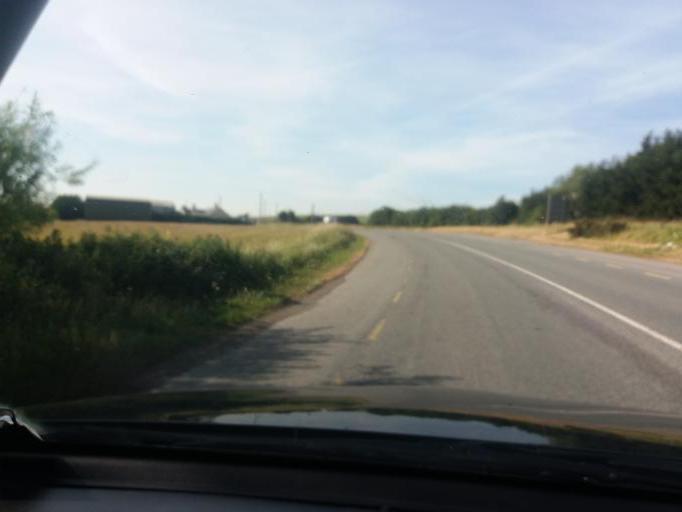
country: IE
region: Leinster
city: Lusk
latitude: 53.5271
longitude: -6.1887
